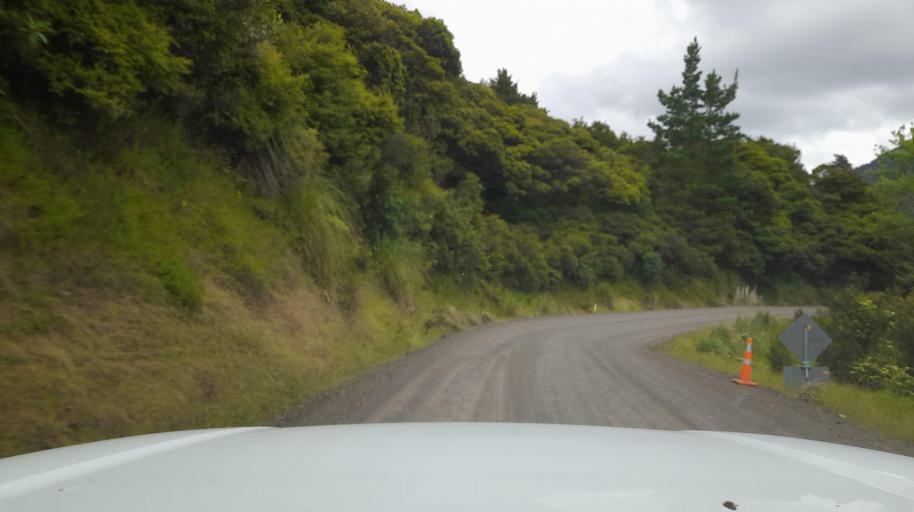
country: NZ
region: Northland
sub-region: Far North District
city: Kaitaia
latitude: -35.3236
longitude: 173.3513
